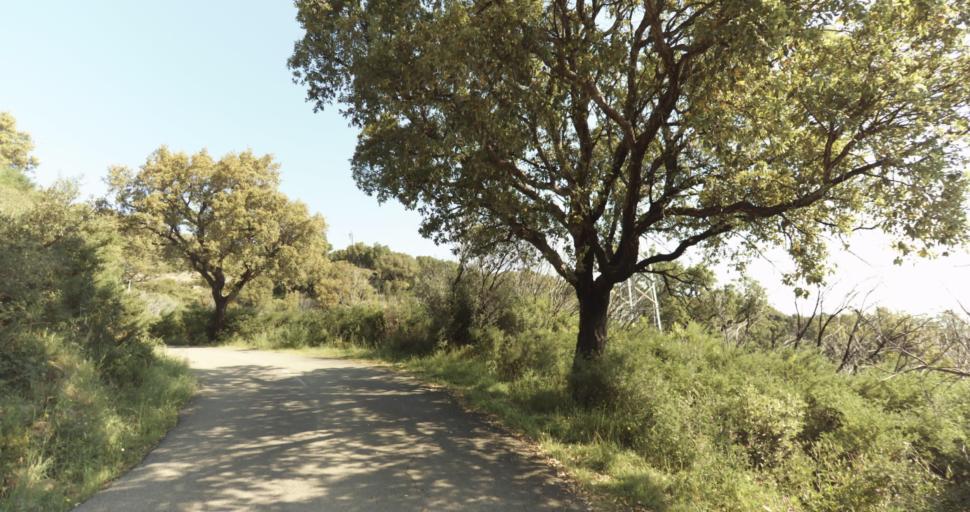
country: FR
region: Corsica
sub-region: Departement de la Haute-Corse
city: Biguglia
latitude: 42.6359
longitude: 9.4168
